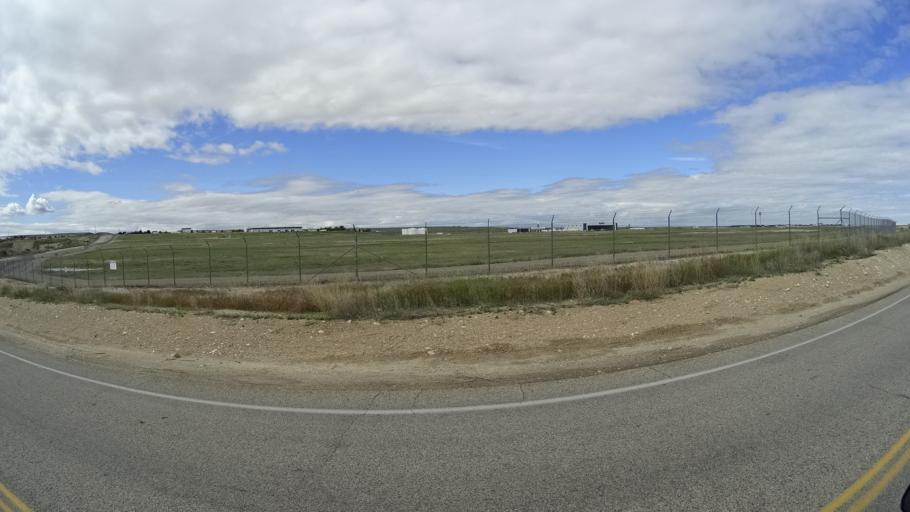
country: US
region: Idaho
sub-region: Ada County
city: Boise
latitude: 43.5546
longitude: -116.1873
